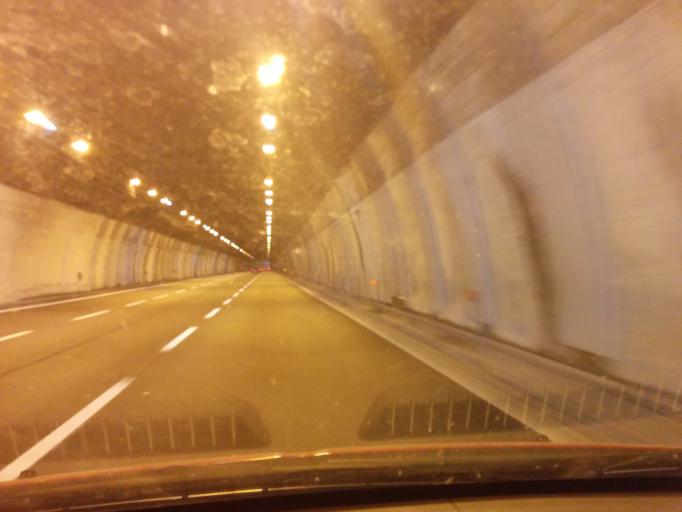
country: IT
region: Liguria
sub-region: Provincia di Genova
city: Mele
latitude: 44.4590
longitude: 8.7447
